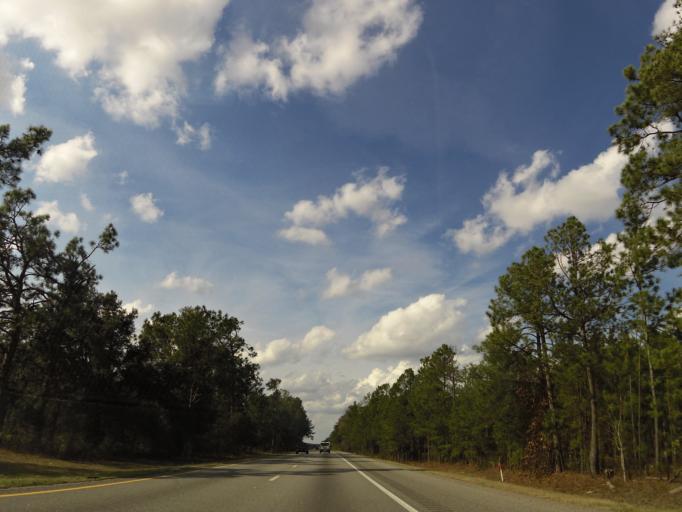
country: US
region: South Carolina
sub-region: Dorchester County
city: Ridgeville
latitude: 33.1724
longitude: -80.3670
